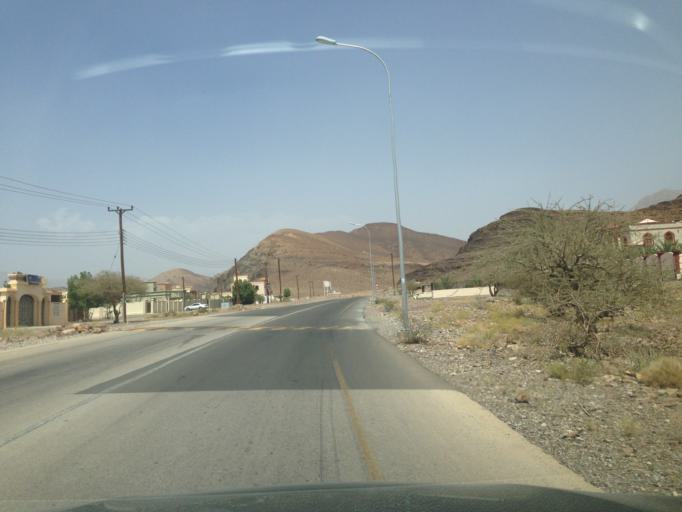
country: OM
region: Muhafazat ad Dakhiliyah
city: Bahla'
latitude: 23.2034
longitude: 56.9465
